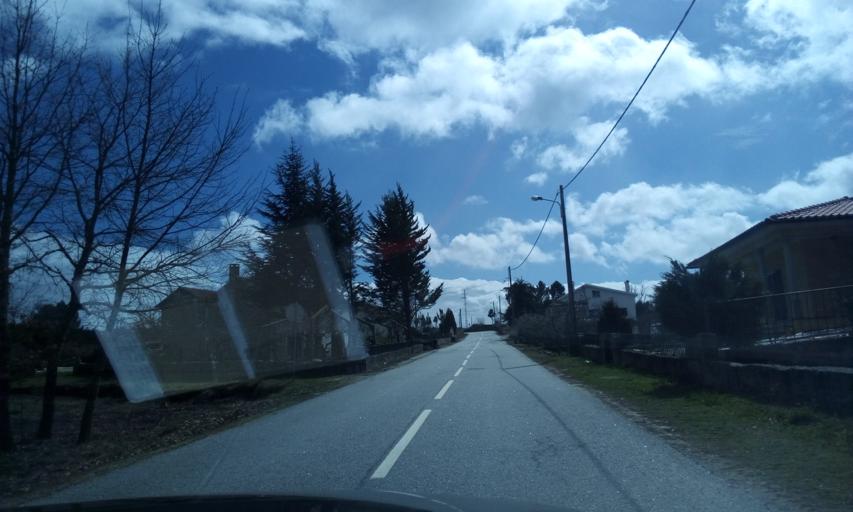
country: PT
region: Guarda
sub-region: Fornos de Algodres
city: Fornos de Algodres
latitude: 40.6417
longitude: -7.5486
